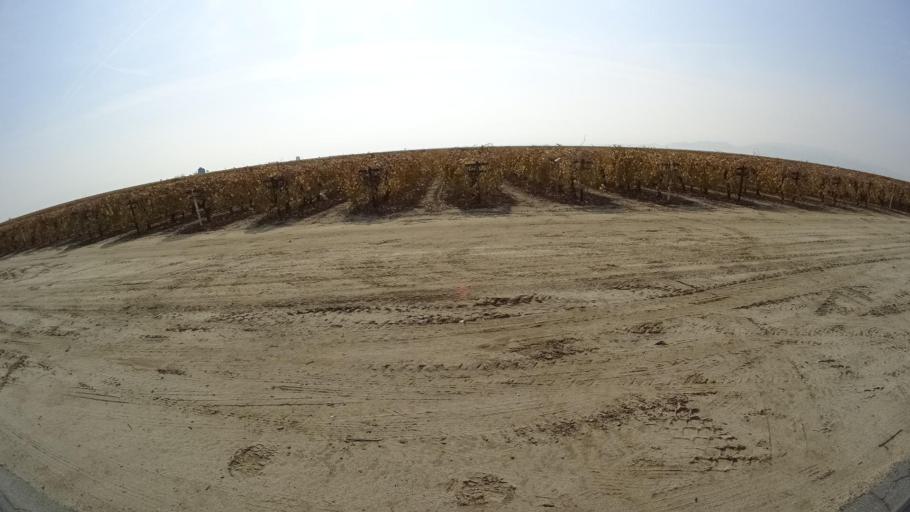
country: US
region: California
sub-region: Kern County
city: Weedpatch
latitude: 35.0744
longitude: -118.9226
